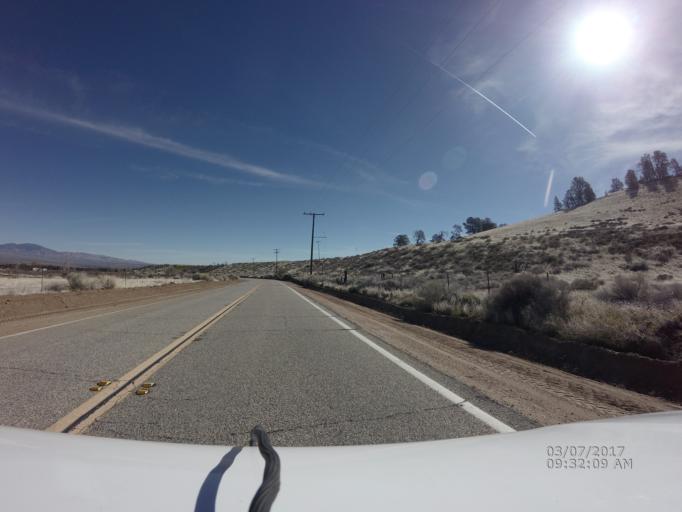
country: US
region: California
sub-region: Los Angeles County
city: Green Valley
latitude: 34.7596
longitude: -118.5975
